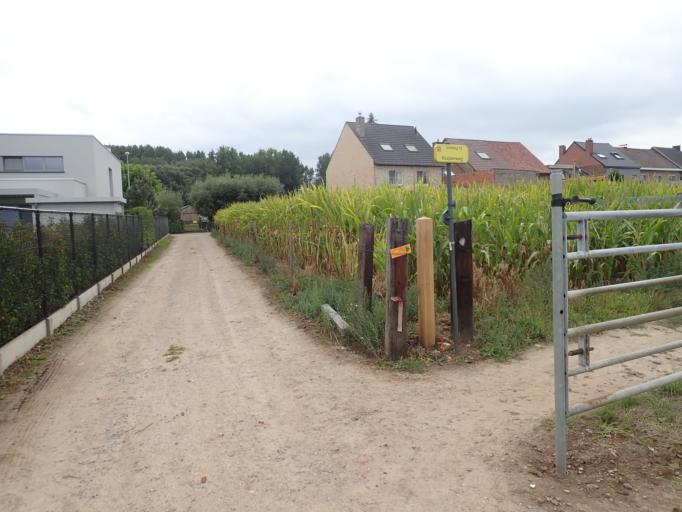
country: BE
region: Flanders
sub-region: Provincie Oost-Vlaanderen
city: Denderleeuw
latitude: 50.9225
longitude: 4.0950
